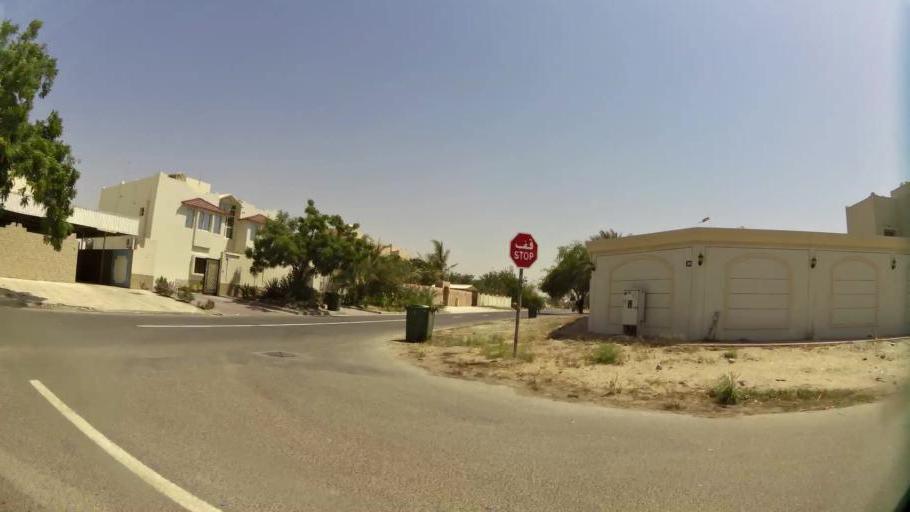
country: AE
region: Ajman
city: Ajman
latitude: 25.4254
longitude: 55.5030
